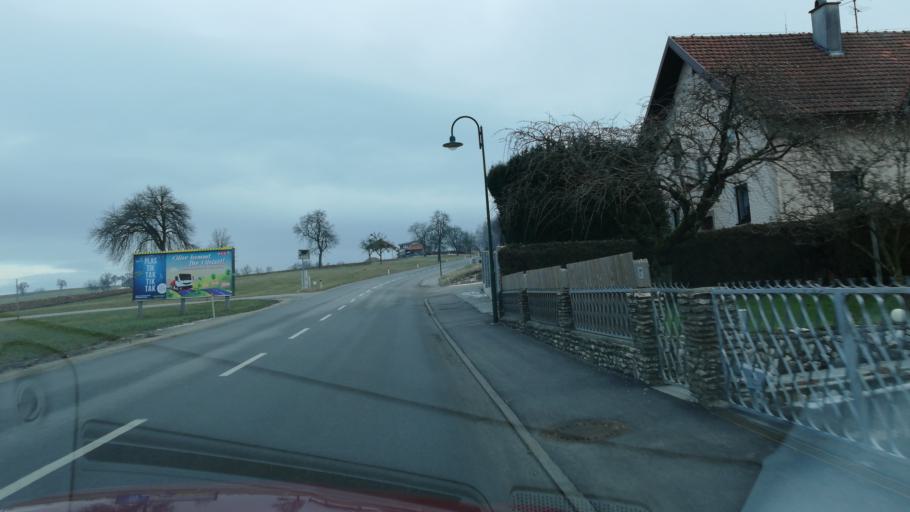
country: AT
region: Upper Austria
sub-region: Politischer Bezirk Vocklabruck
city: Niederthalheim
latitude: 48.1860
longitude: 13.7485
